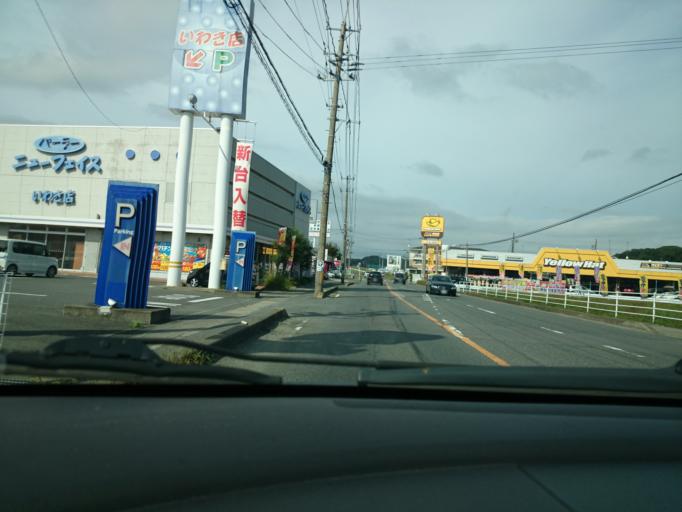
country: JP
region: Fukushima
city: Iwaki
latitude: 36.9695
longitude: 140.8913
